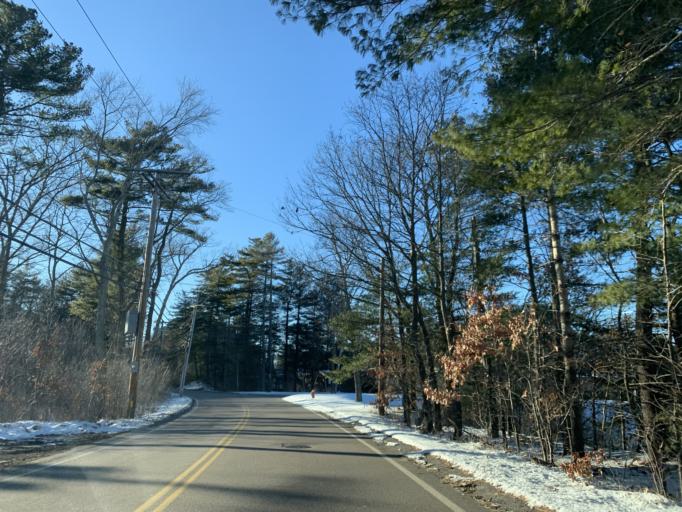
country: US
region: Massachusetts
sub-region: Norfolk County
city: Walpole
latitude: 42.1114
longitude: -71.2458
